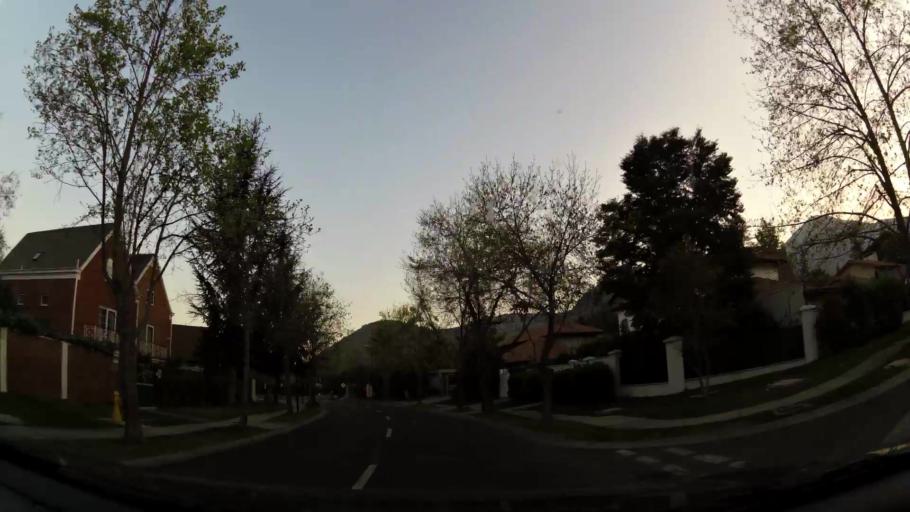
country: CL
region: Santiago Metropolitan
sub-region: Provincia de Chacabuco
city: Chicureo Abajo
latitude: -33.3367
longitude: -70.5522
